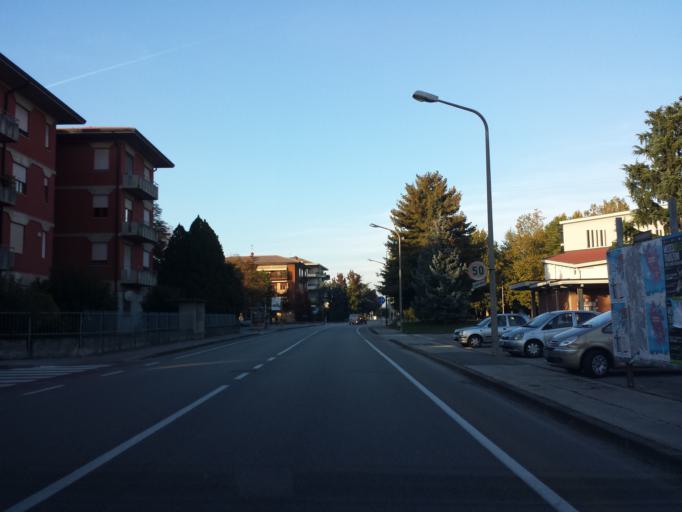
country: IT
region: Veneto
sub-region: Provincia di Vicenza
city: Vicenza
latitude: 45.5725
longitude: 11.5442
